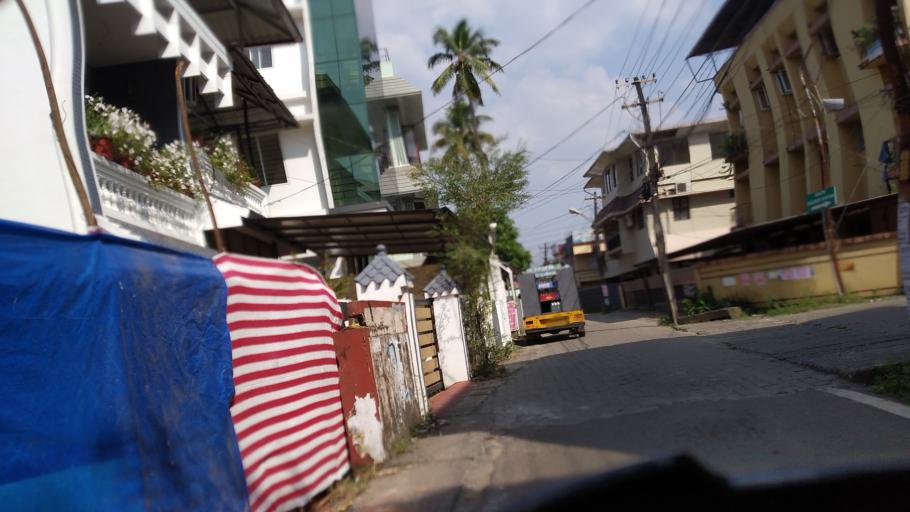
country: IN
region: Kerala
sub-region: Ernakulam
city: Cochin
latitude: 9.9740
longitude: 76.2893
